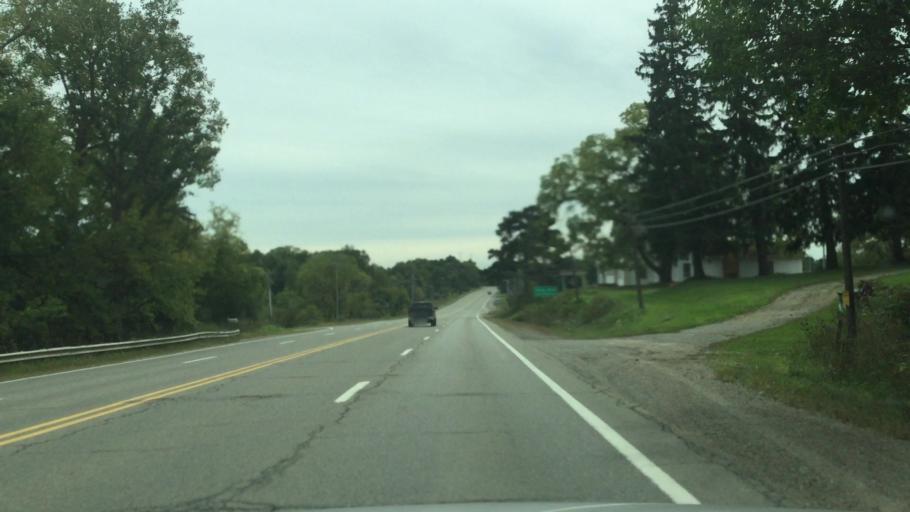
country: US
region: Michigan
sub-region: Oakland County
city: Ortonville
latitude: 42.7825
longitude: -83.5014
